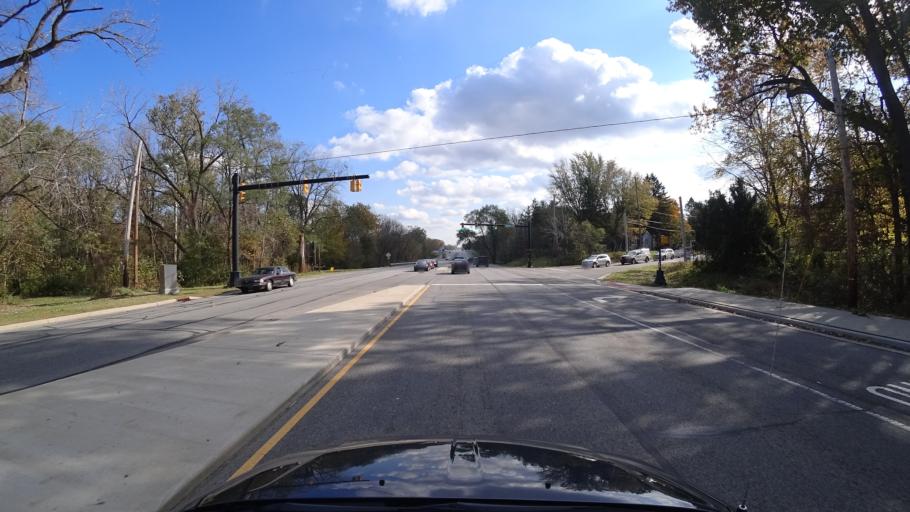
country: US
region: Indiana
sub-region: LaPorte County
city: Trail Creek
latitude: 41.7059
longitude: -86.8585
